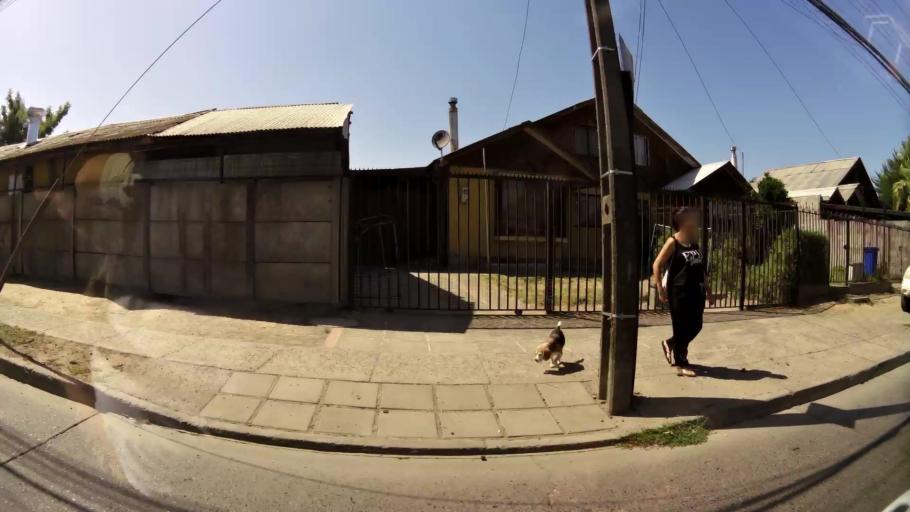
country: CL
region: Maule
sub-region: Provincia de Talca
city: Talca
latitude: -35.4185
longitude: -71.6437
